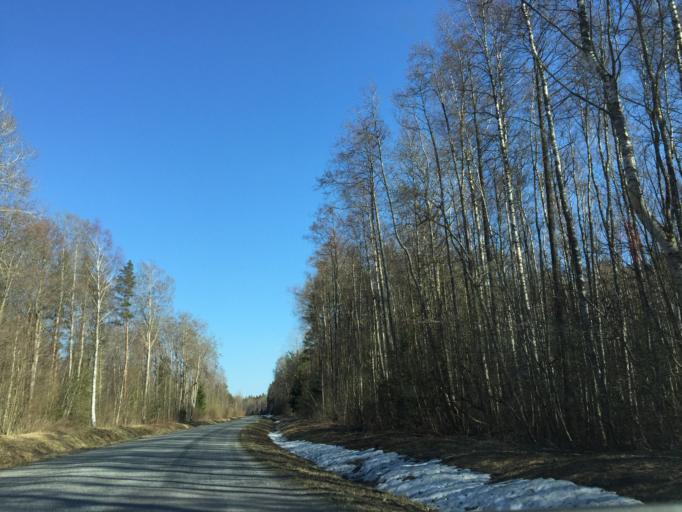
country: RU
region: Pskov
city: Gdov
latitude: 59.0121
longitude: 27.6039
